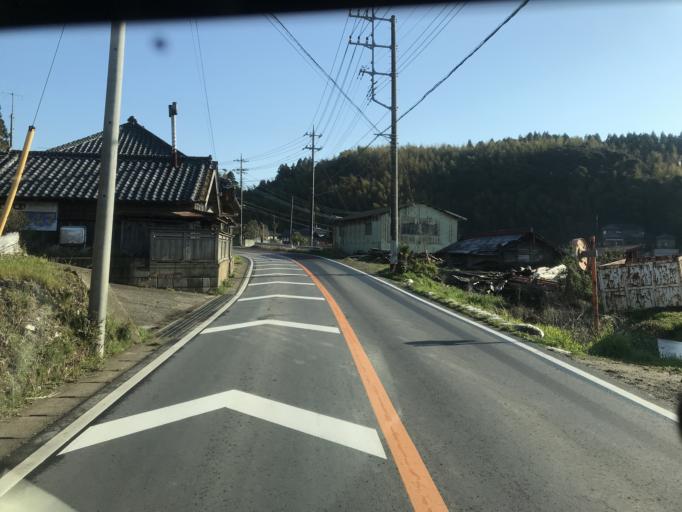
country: JP
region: Chiba
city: Sawara
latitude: 35.8768
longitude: 140.4955
